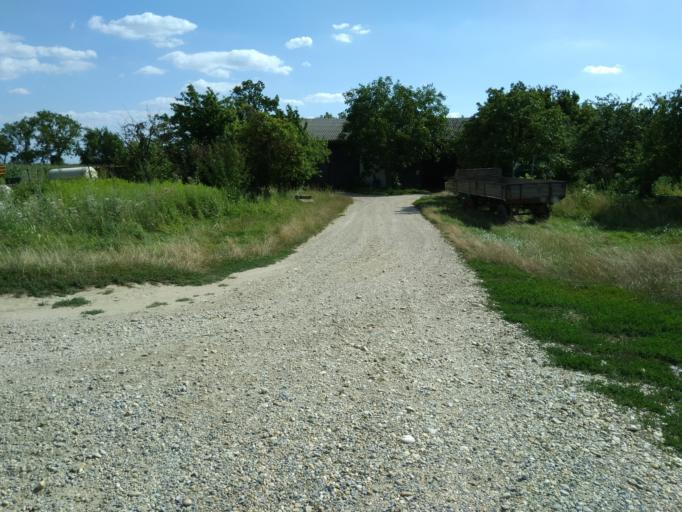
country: AT
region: Lower Austria
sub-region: Politischer Bezirk Mistelbach
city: Pillichsdorf
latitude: 48.3625
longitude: 16.5354
